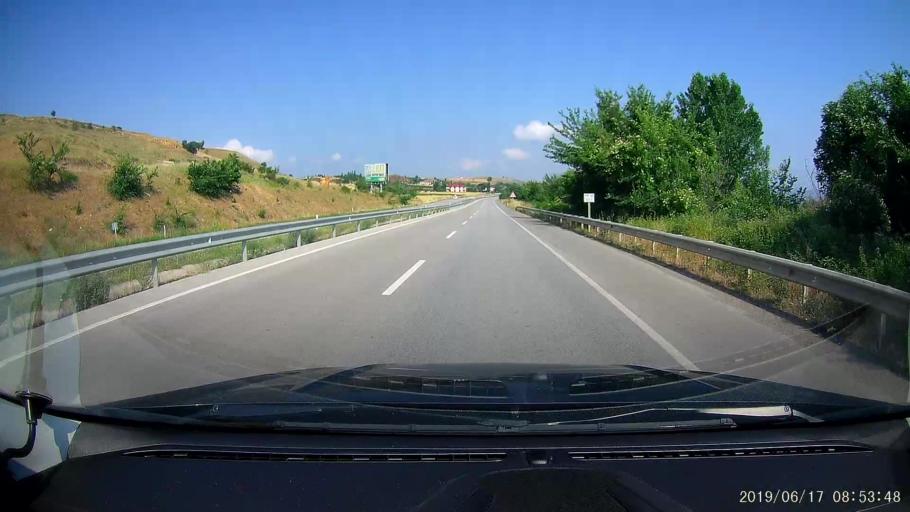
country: TR
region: Tokat
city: Erbaa
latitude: 40.7129
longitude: 36.4740
